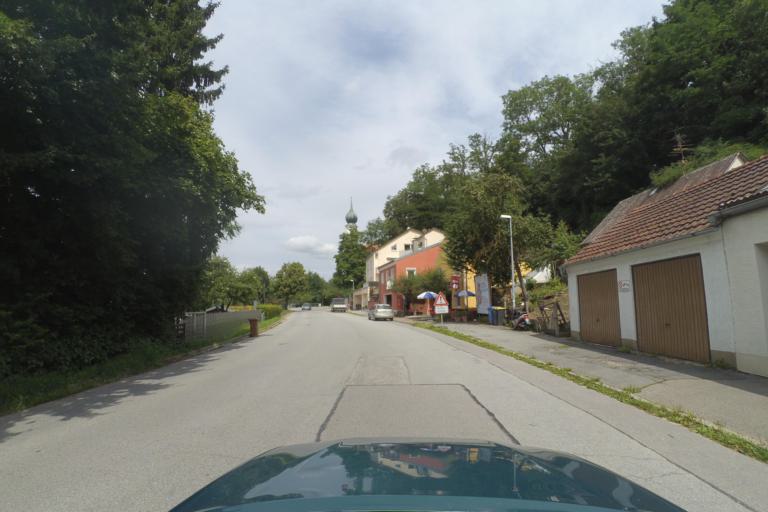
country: DE
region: Bavaria
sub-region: Lower Bavaria
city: Landau an der Isar
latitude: 48.6736
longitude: 12.6982
